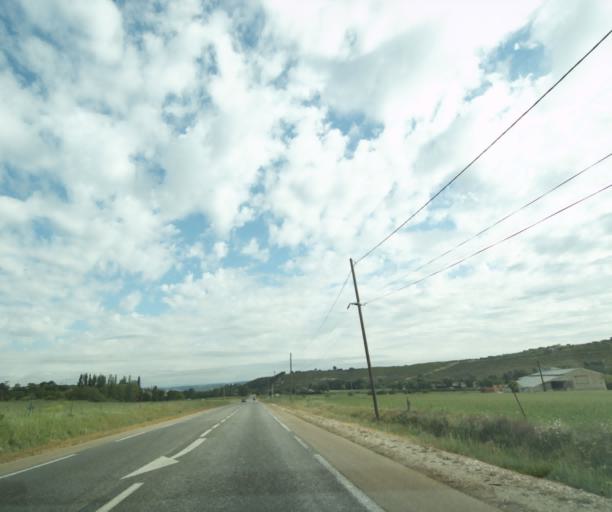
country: FR
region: Provence-Alpes-Cote d'Azur
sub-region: Departement des Bouches-du-Rhone
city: Cabries
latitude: 43.4706
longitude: 5.3546
